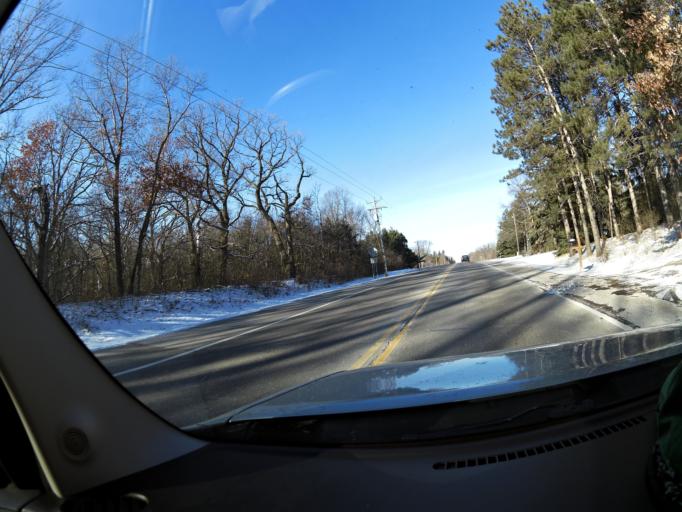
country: US
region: Minnesota
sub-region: Washington County
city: Lake Elmo
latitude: 44.9230
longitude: -92.8626
